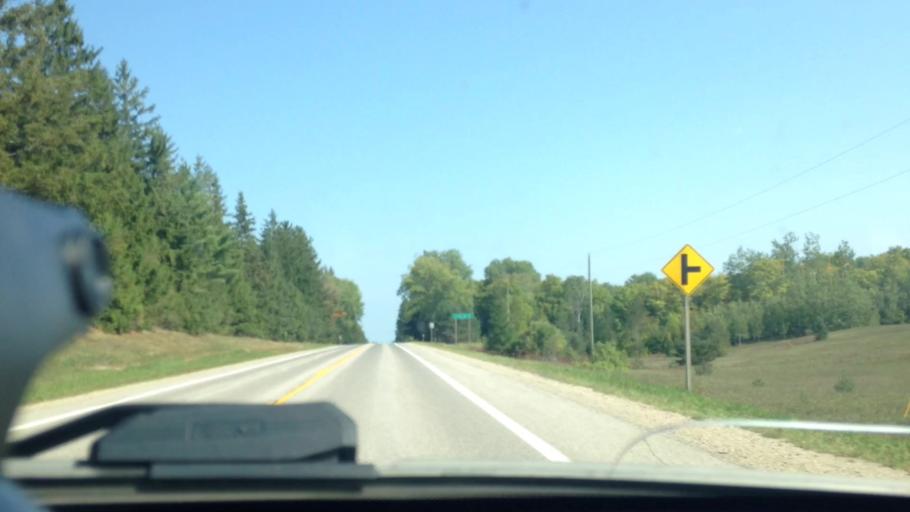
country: US
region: Michigan
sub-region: Luce County
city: Newberry
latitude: 46.3037
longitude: -85.4409
